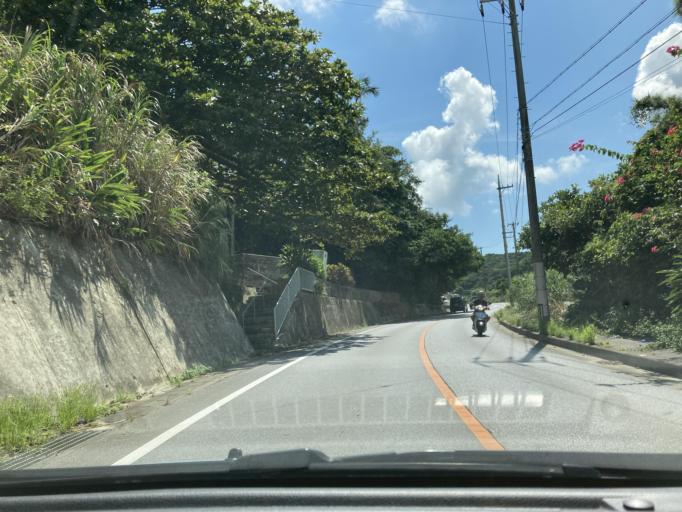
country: JP
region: Okinawa
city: Tomigusuku
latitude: 26.1623
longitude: 127.7625
